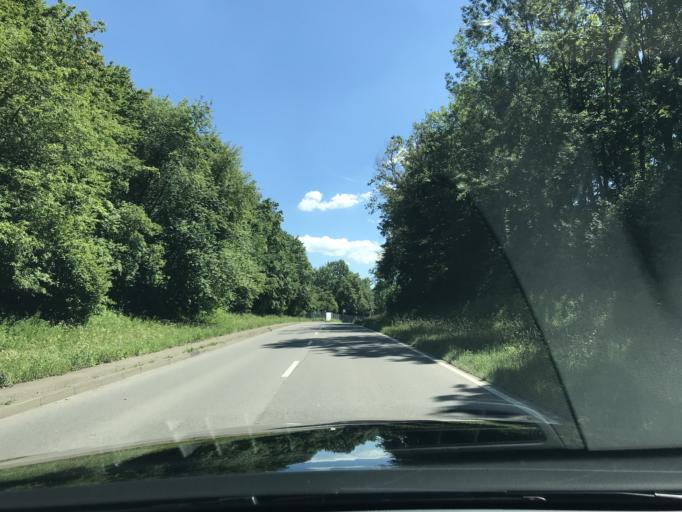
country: DE
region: Baden-Wuerttemberg
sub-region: Regierungsbezirk Stuttgart
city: Korb
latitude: 48.8394
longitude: 9.3409
